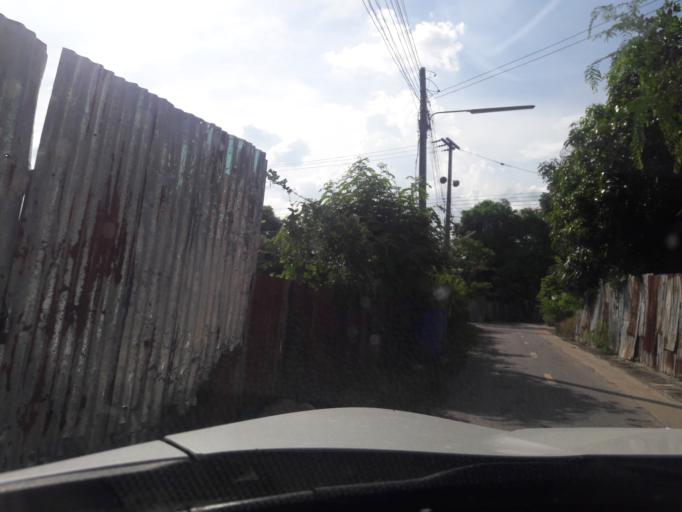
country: TH
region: Lop Buri
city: Ban Mi
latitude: 15.0533
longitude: 100.5474
